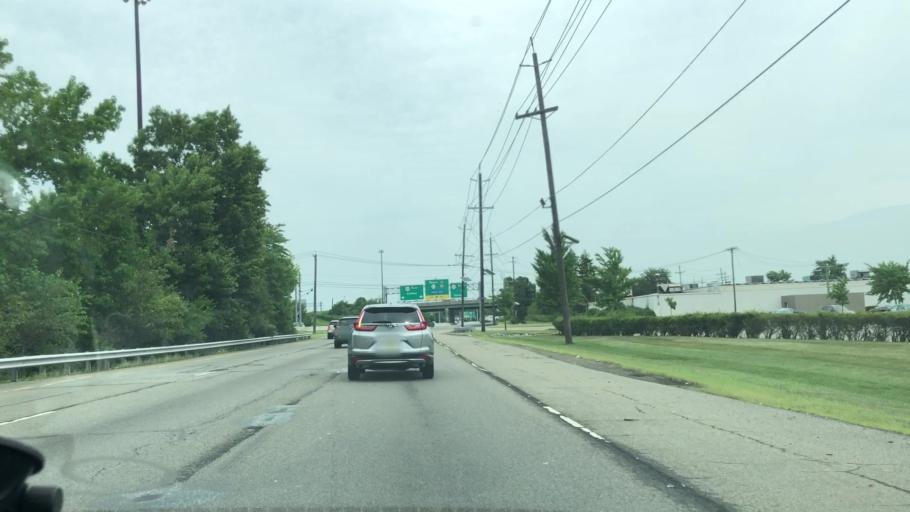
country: US
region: New Jersey
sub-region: Passaic County
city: Singac
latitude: 40.8930
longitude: -74.2587
